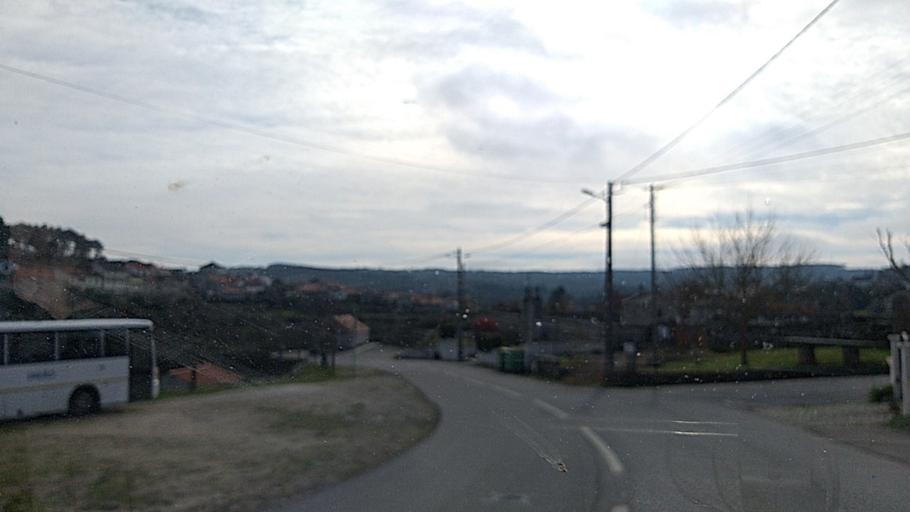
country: PT
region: Guarda
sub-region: Fornos de Algodres
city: Fornos de Algodres
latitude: 40.6829
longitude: -7.5337
